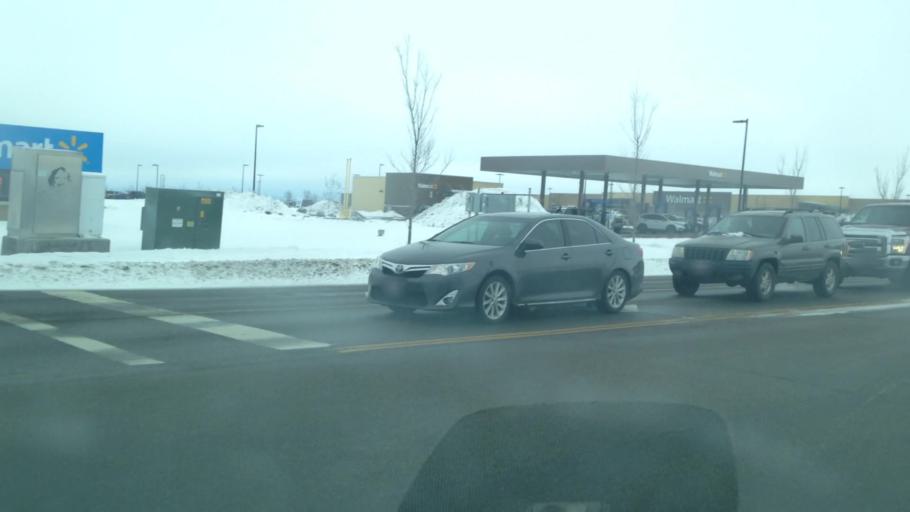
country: US
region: Idaho
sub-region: Madison County
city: Rexburg
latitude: 43.8548
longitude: -111.7777
